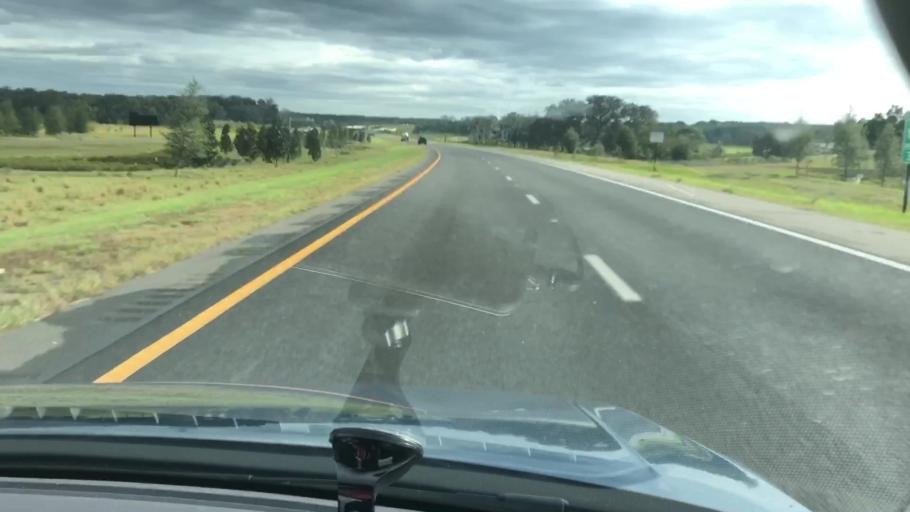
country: US
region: Florida
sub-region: Orange County
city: Zellwood
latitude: 28.7429
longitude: -81.5668
